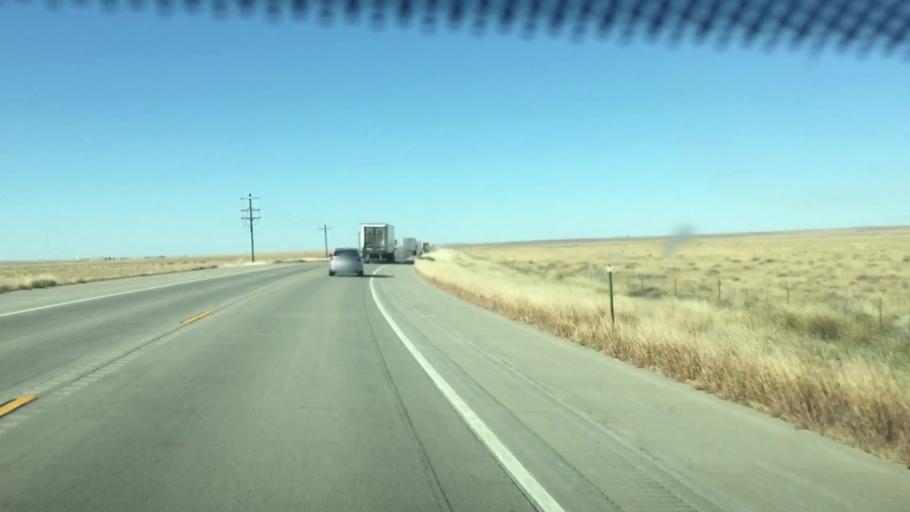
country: US
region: Colorado
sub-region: Kiowa County
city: Eads
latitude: 38.3759
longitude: -102.7301
